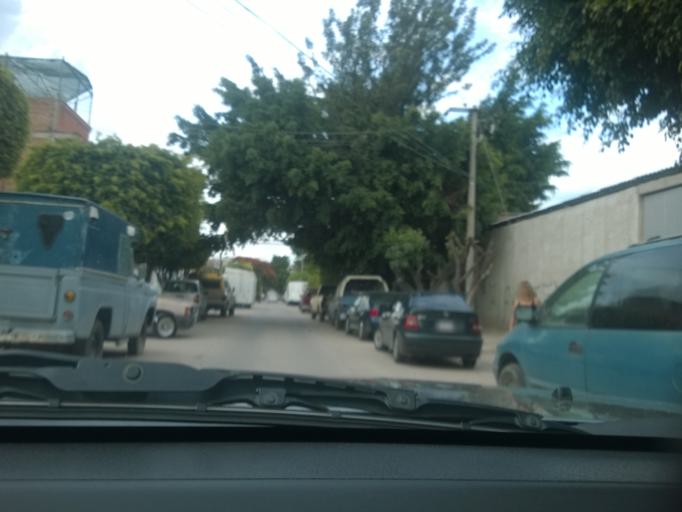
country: MX
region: Guanajuato
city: Leon
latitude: 21.1268
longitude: -101.6982
